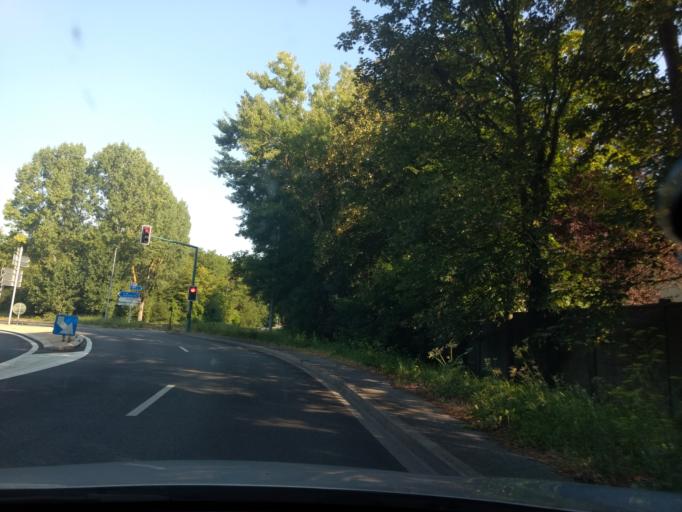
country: FR
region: Ile-de-France
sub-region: Departement des Yvelines
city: Velizy-Villacoublay
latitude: 48.7789
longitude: 2.1779
